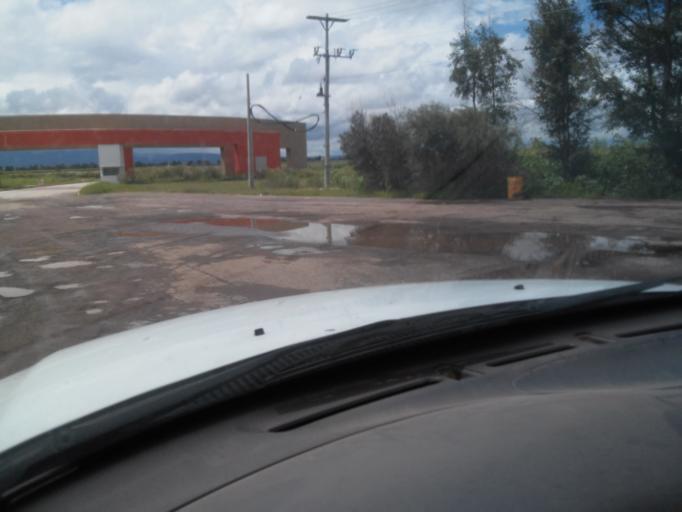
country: MX
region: Durango
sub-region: Durango
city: Jose Refugio Salcido
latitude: 24.0180
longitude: -104.5469
